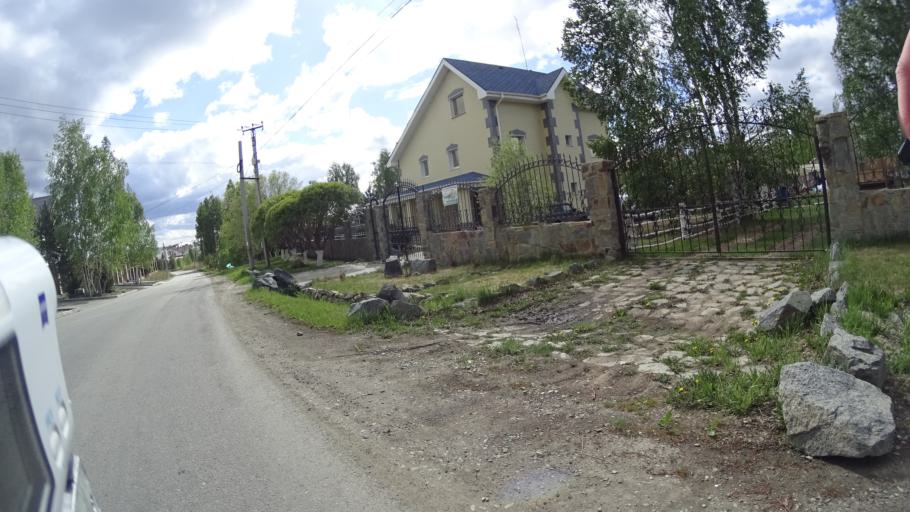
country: RU
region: Chelyabinsk
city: Sargazy
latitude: 55.1585
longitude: 61.2428
